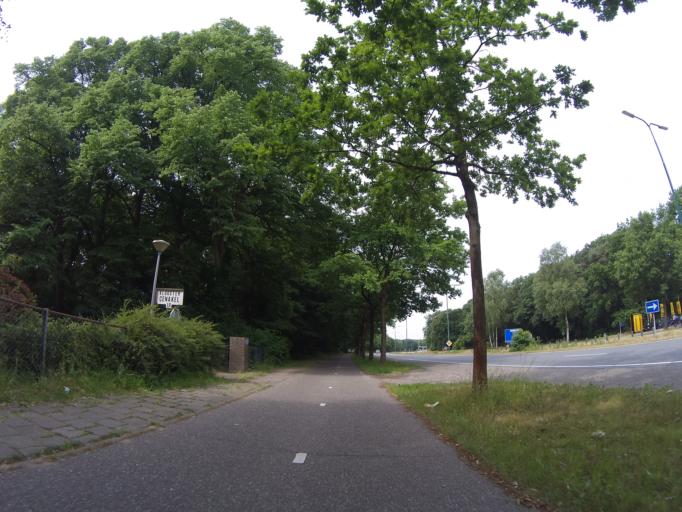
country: NL
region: Utrecht
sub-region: Gemeente Soest
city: Soest
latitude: 52.1238
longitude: 5.2962
